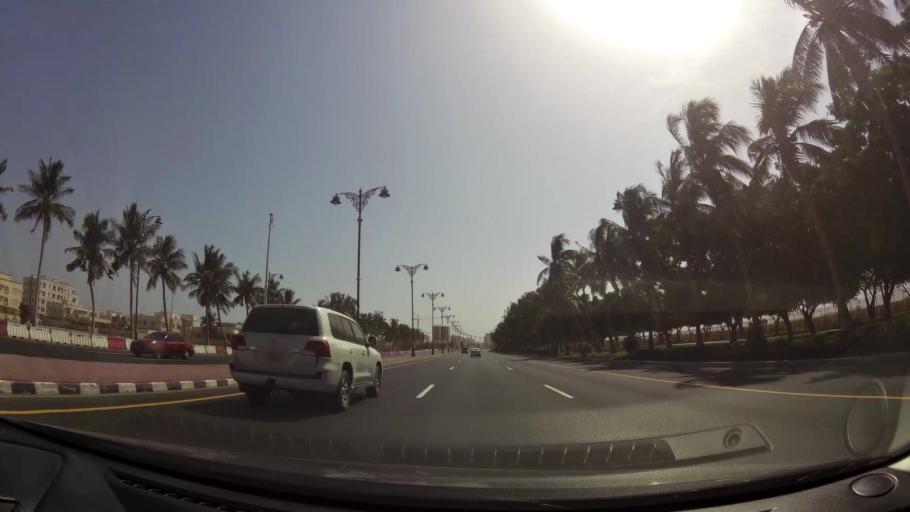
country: OM
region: Zufar
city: Salalah
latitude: 17.0241
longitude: 54.1072
